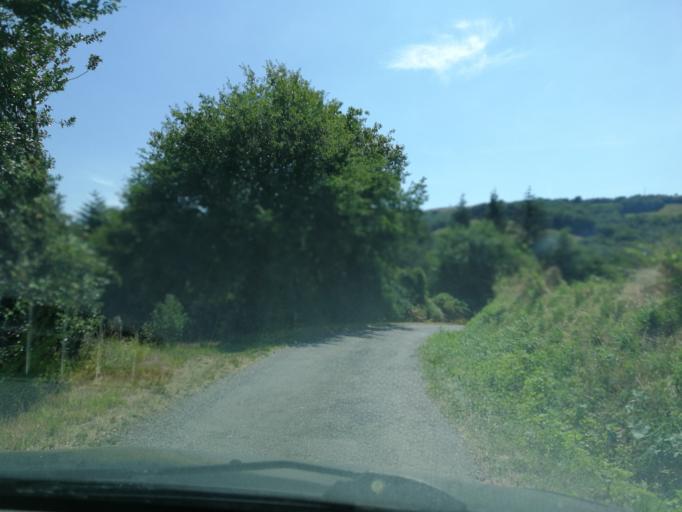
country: FR
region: Auvergne
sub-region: Departement du Cantal
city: Maurs
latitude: 44.6878
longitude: 2.3293
